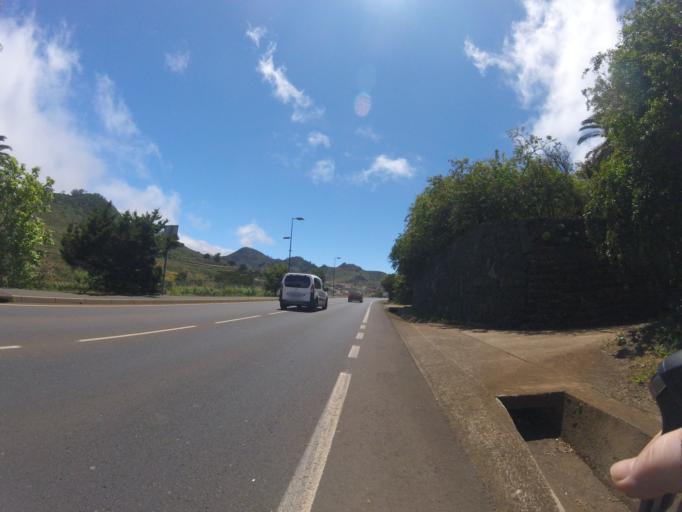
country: ES
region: Canary Islands
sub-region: Provincia de Santa Cruz de Tenerife
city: Tegueste
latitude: 28.5192
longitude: -16.3281
